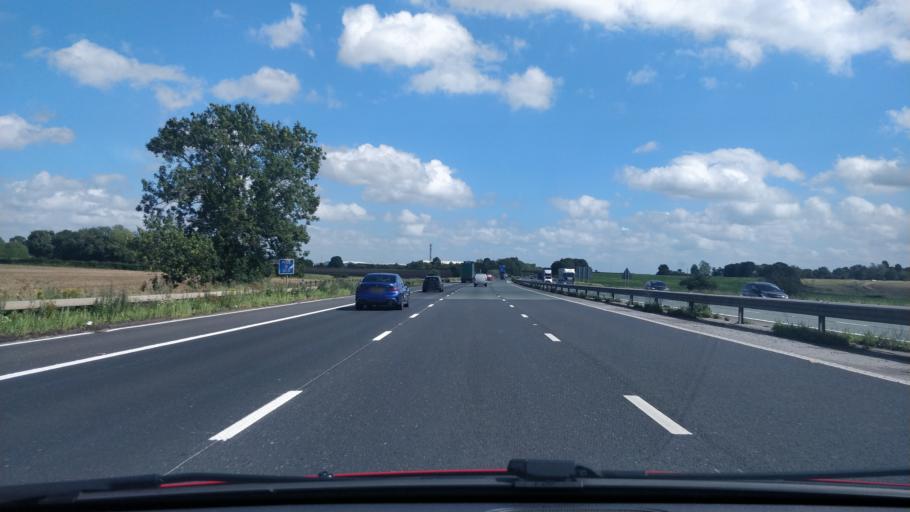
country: GB
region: England
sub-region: Warrington
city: Appleton Thorn
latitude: 53.3431
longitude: -2.5463
